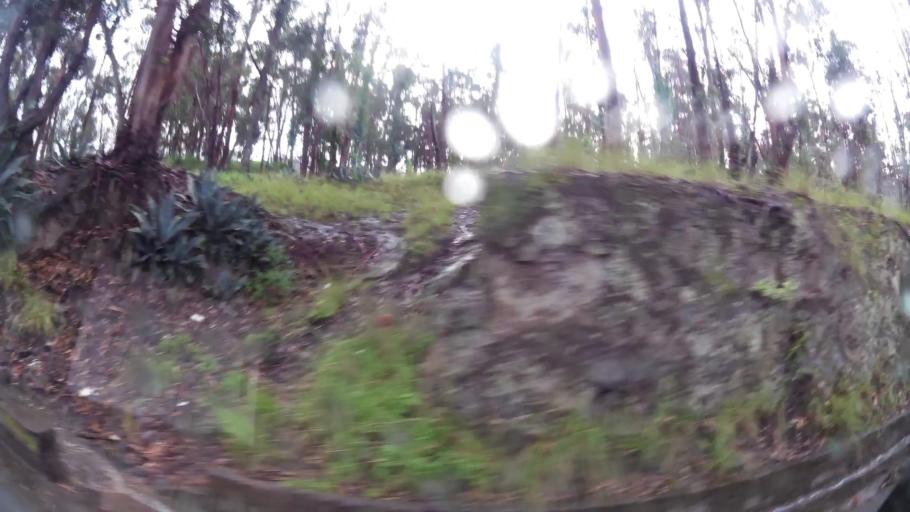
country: EC
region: Pichincha
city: Quito
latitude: -0.0921
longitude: -78.4978
